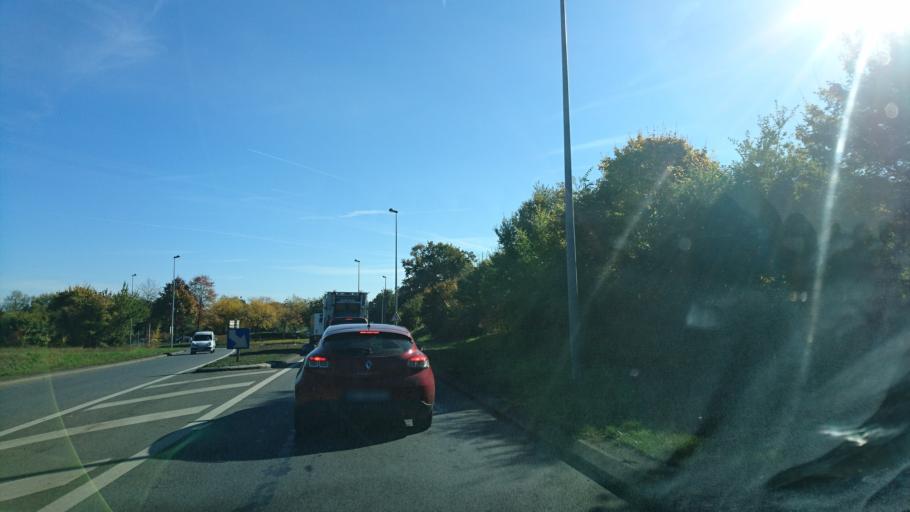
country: FR
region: Brittany
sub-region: Departement d'Ille-et-Vilaine
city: Chartres-de-Bretagne
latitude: 48.0434
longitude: -1.6972
